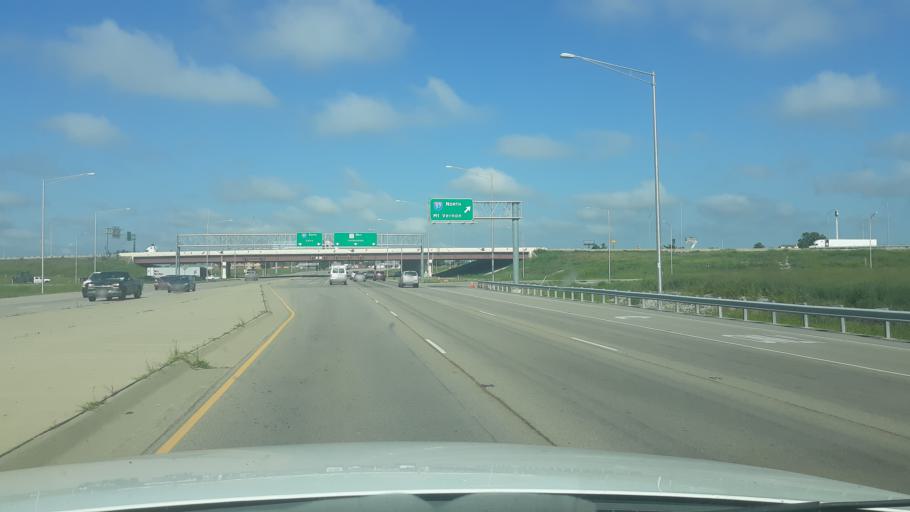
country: US
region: Illinois
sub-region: Williamson County
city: Marion
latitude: 37.7407
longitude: -88.9549
